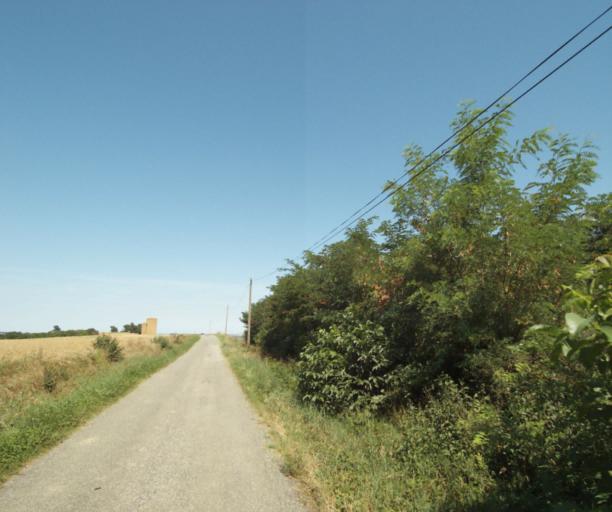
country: FR
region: Midi-Pyrenees
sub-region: Departement de l'Ariege
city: Lezat-sur-Leze
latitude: 43.2610
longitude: 1.3881
